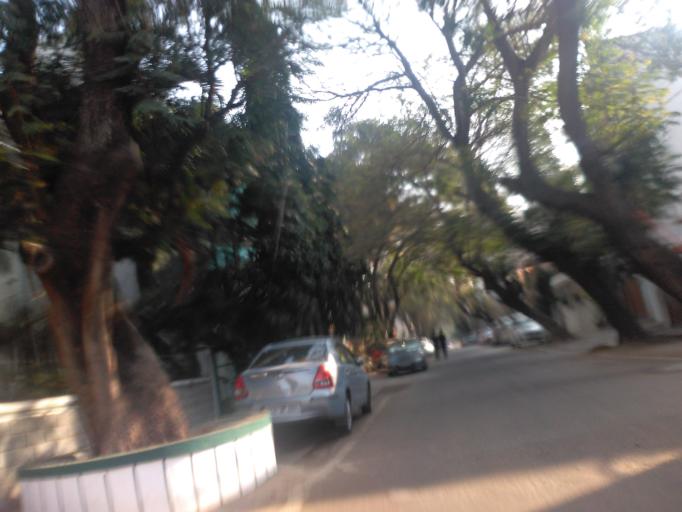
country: IN
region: Karnataka
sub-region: Bangalore Urban
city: Bangalore
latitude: 12.9763
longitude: 77.6527
